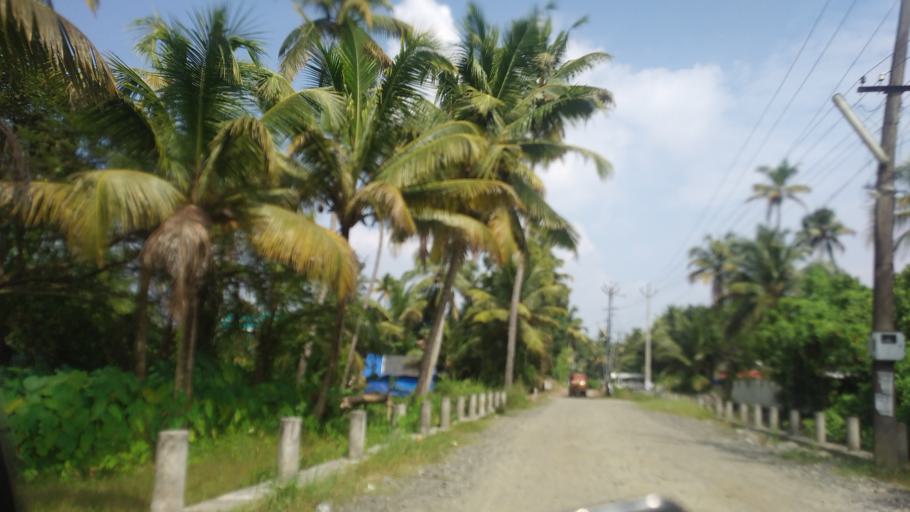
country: IN
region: Kerala
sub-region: Ernakulam
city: Elur
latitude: 10.0773
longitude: 76.2047
